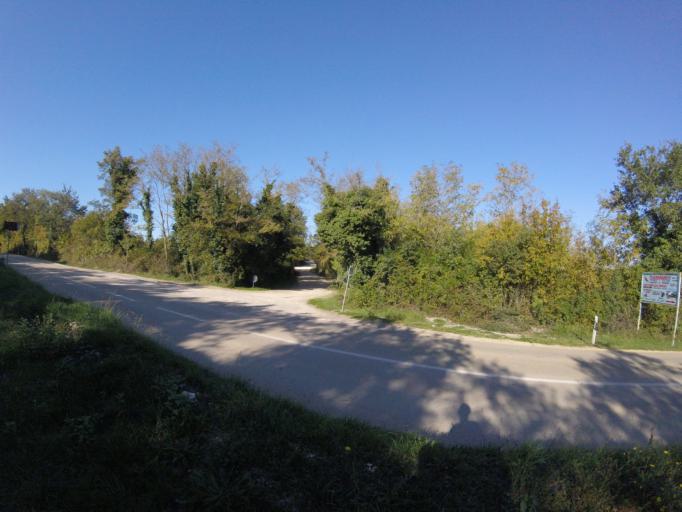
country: HR
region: Istarska
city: Vrsar
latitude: 45.1516
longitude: 13.6225
